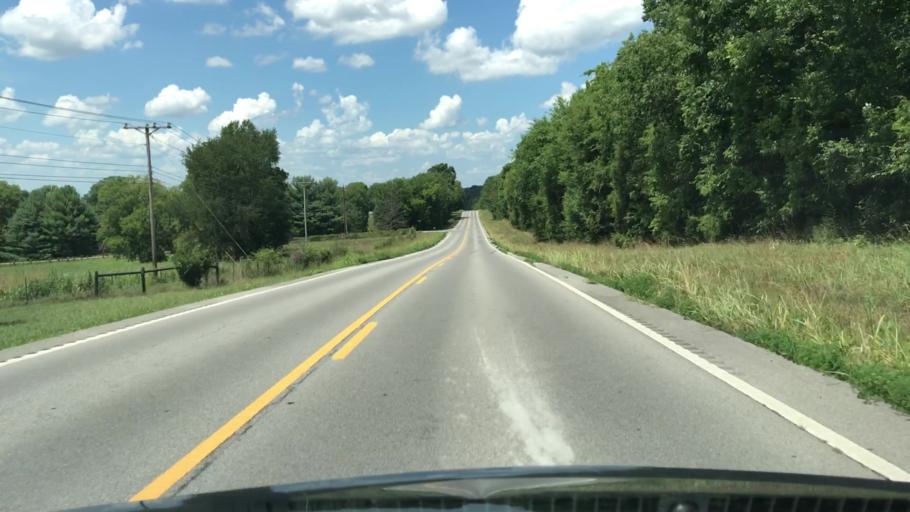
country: US
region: Tennessee
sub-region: Williamson County
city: Nolensville
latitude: 35.8518
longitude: -86.6248
